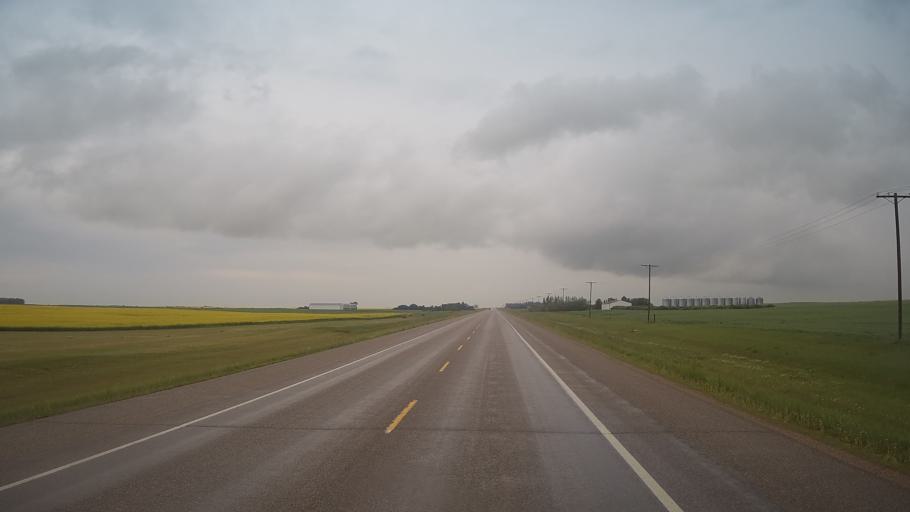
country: CA
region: Saskatchewan
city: Wilkie
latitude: 52.4056
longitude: -108.7626
